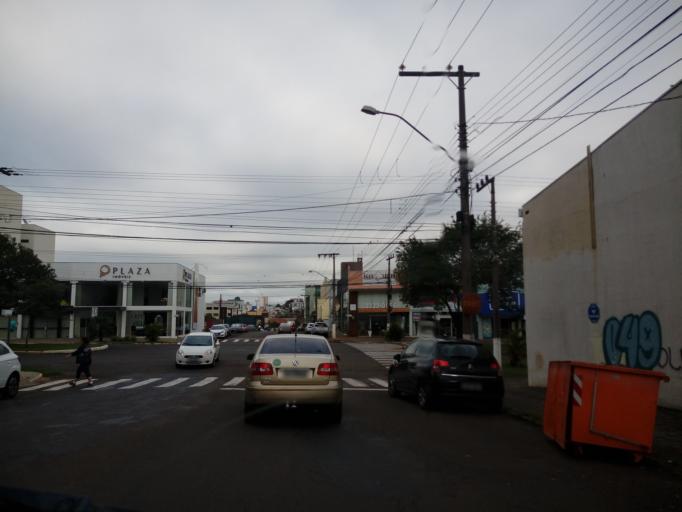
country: BR
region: Santa Catarina
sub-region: Chapeco
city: Chapeco
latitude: -27.0909
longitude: -52.6178
